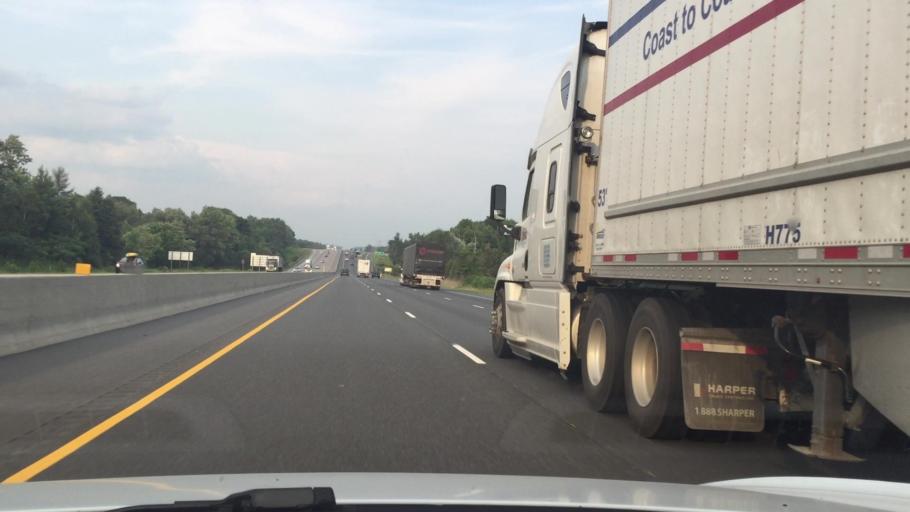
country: CA
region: Ontario
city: Cobourg
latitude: 43.9281
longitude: -78.5022
